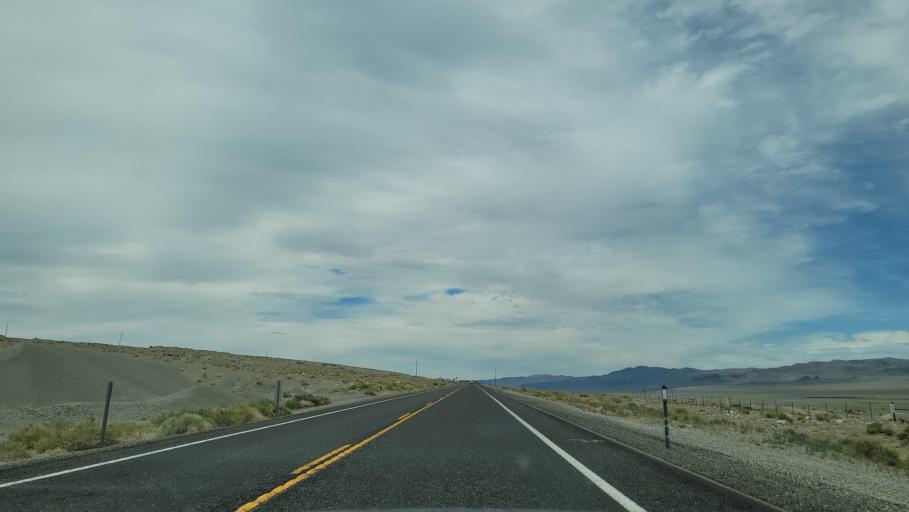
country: US
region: Nevada
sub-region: Mineral County
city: Hawthorne
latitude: 38.5904
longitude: -118.7086
